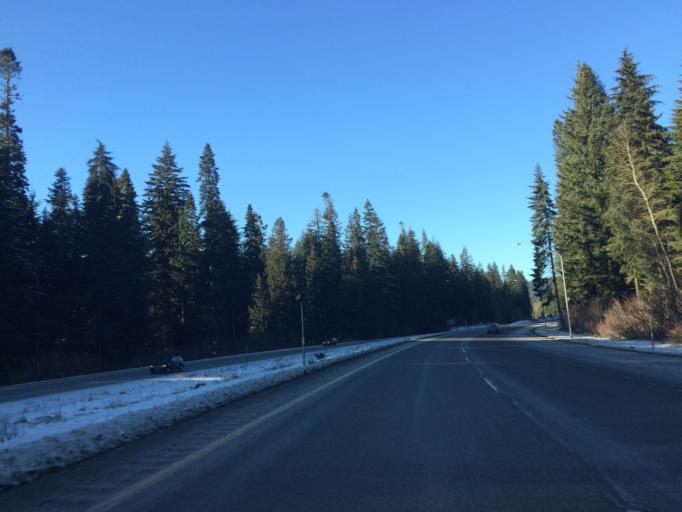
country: US
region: Washington
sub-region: Kittitas County
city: Cle Elum
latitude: 47.3087
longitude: -121.3111
